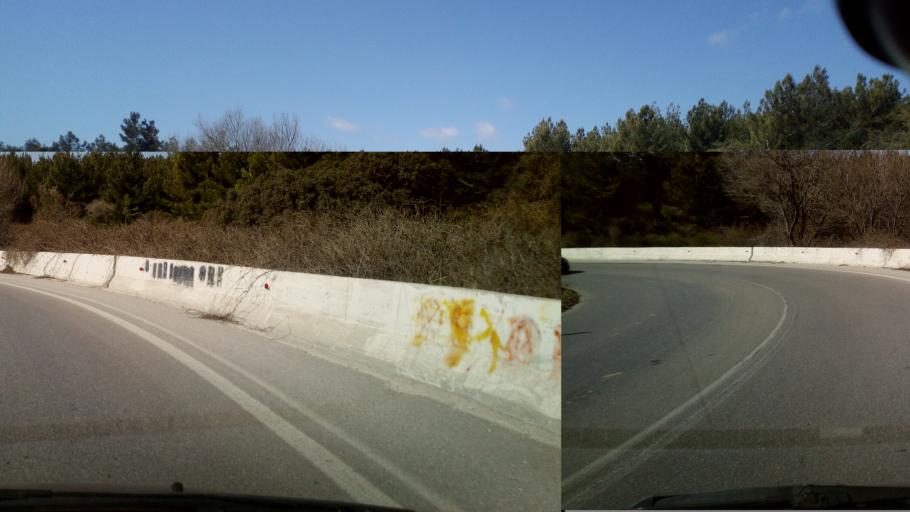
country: GR
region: Central Macedonia
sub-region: Nomos Thessalonikis
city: Panorama
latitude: 40.6132
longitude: 23.0587
